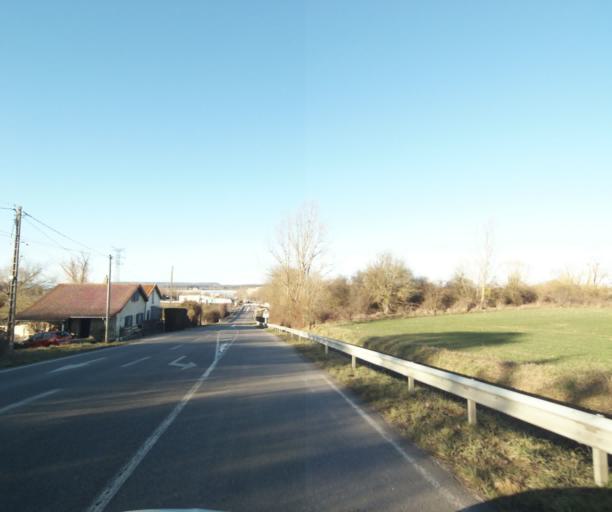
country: FR
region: Lorraine
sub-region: Departement de Meurthe-et-Moselle
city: Art-sur-Meurthe
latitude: 48.6390
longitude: 6.2540
